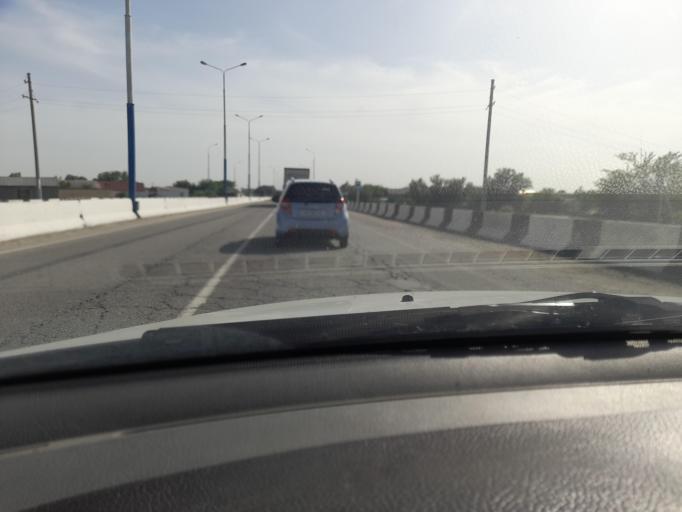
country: UZ
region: Samarqand
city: Kattaqo'rg'on
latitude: 39.9269
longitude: 66.3590
